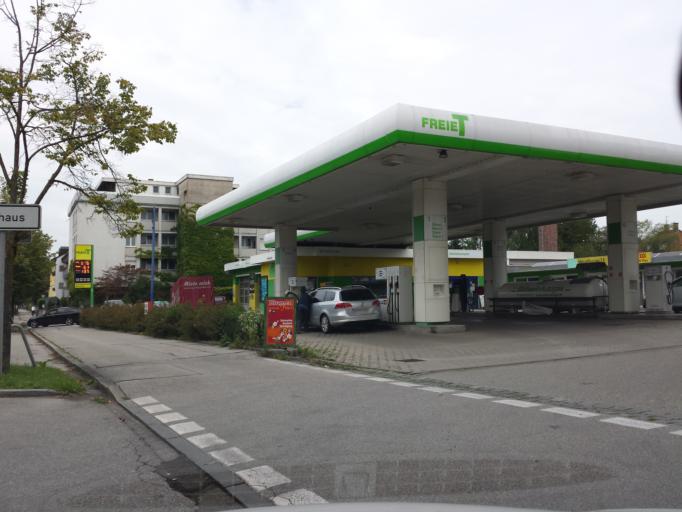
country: DE
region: Bavaria
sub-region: Upper Bavaria
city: Freilassing
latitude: 47.8423
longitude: 12.9768
